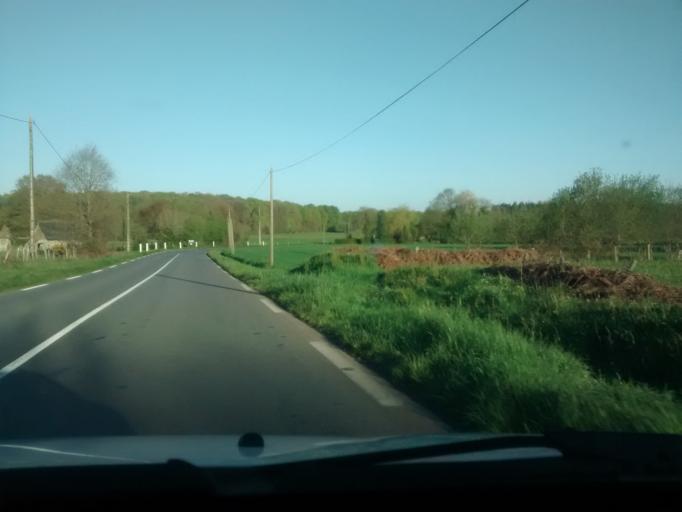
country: FR
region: Brittany
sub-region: Departement d'Ille-et-Vilaine
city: Antrain
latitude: 48.4673
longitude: -1.5274
